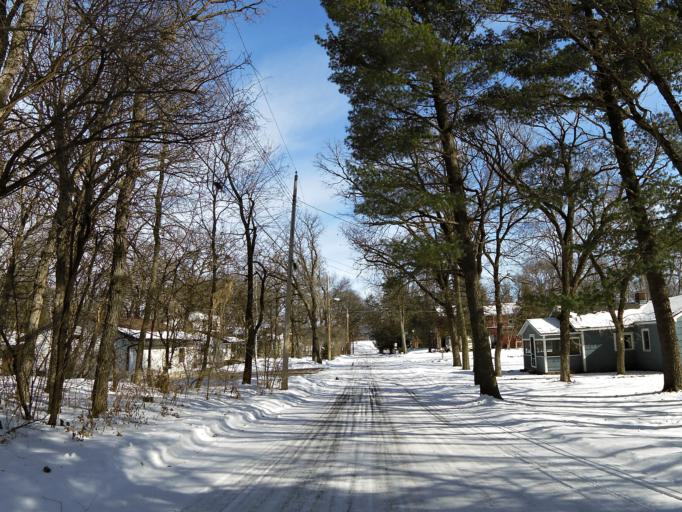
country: US
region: Minnesota
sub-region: Washington County
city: Lake Saint Croix Beach
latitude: 44.9229
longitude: -92.7667
